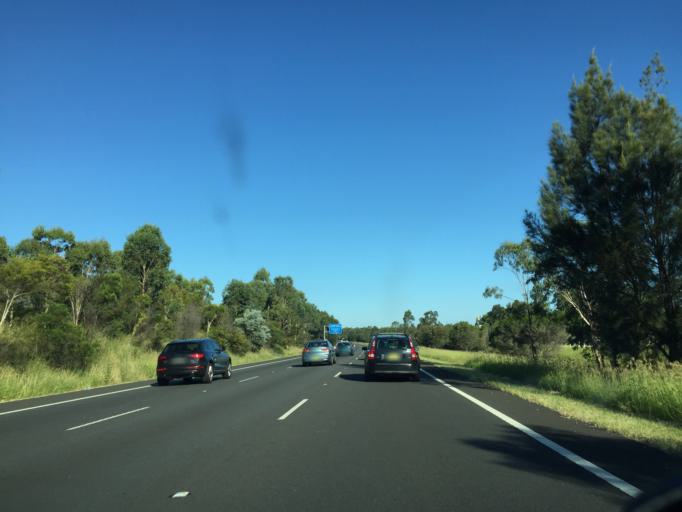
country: AU
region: New South Wales
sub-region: Penrith Municipality
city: Glenmore Park
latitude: -33.7798
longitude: 150.6823
